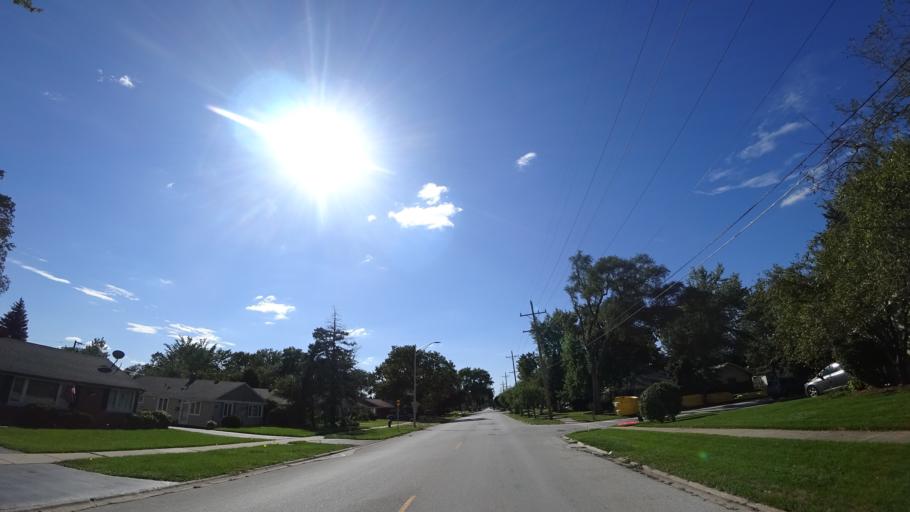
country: US
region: Illinois
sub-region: Cook County
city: Oak Lawn
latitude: 41.7127
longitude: -87.7486
